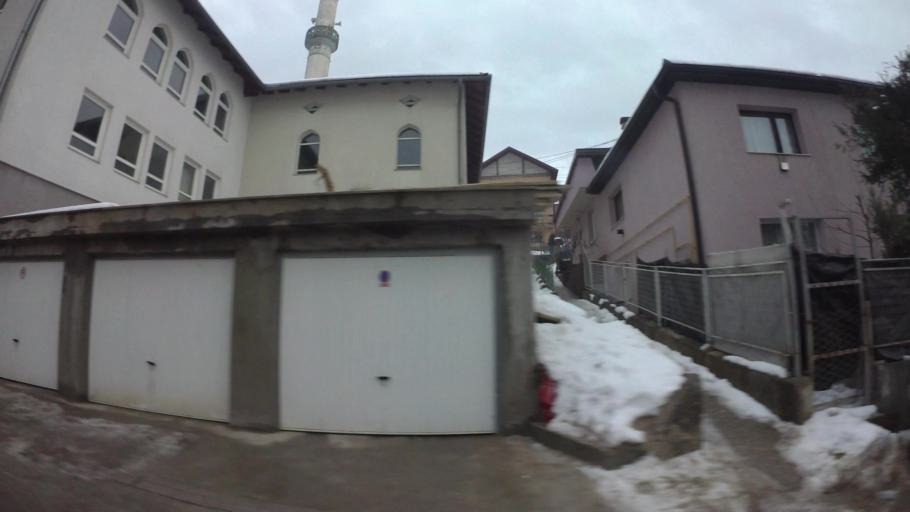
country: BA
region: Federation of Bosnia and Herzegovina
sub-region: Kanton Sarajevo
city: Sarajevo
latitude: 43.8570
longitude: 18.3458
